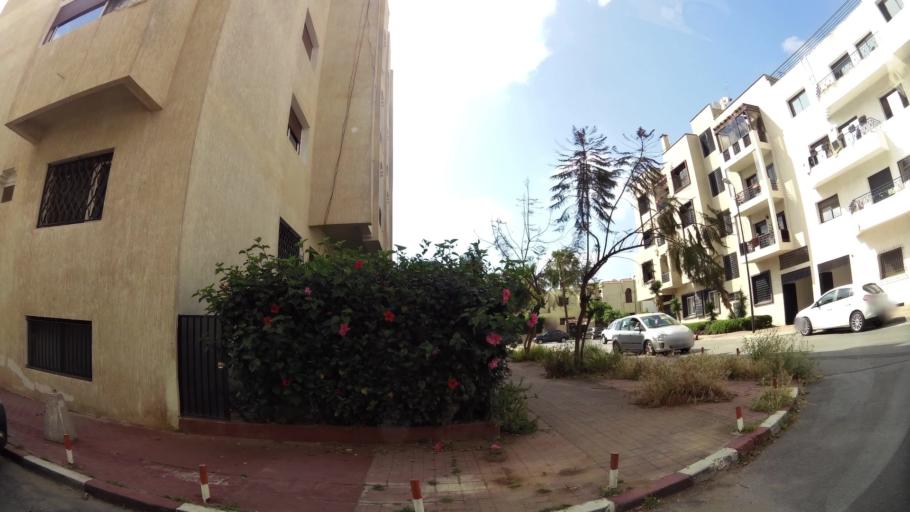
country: MA
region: Rabat-Sale-Zemmour-Zaer
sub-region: Skhirate-Temara
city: Temara
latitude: 33.9602
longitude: -6.8692
